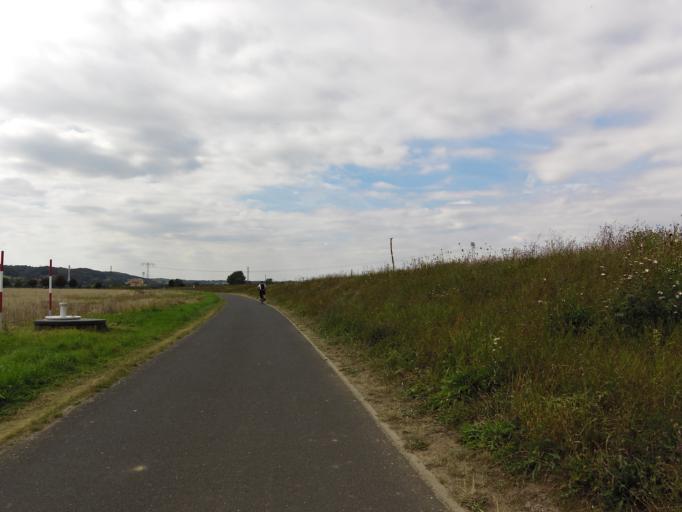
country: DE
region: Saxony
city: Radebeul
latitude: 51.0995
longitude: 13.6280
